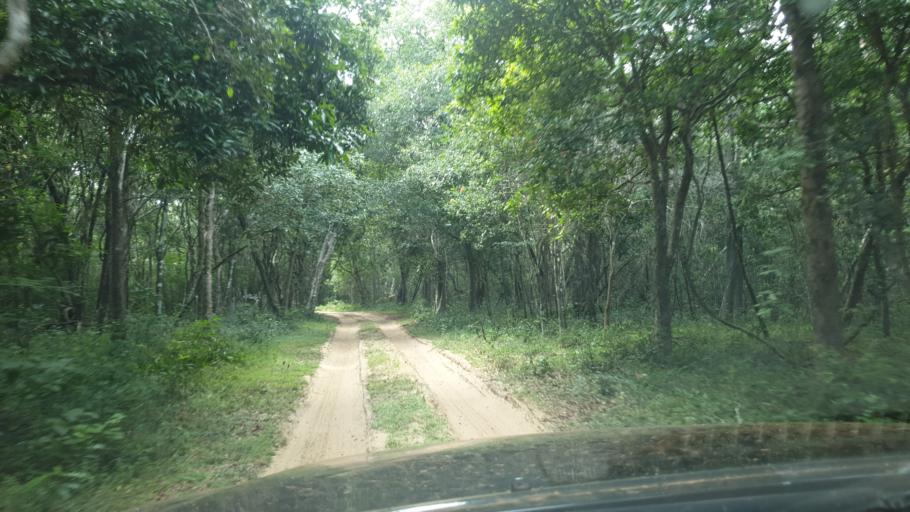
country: LK
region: North Western
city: Puttalam
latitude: 8.4145
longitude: 79.9950
